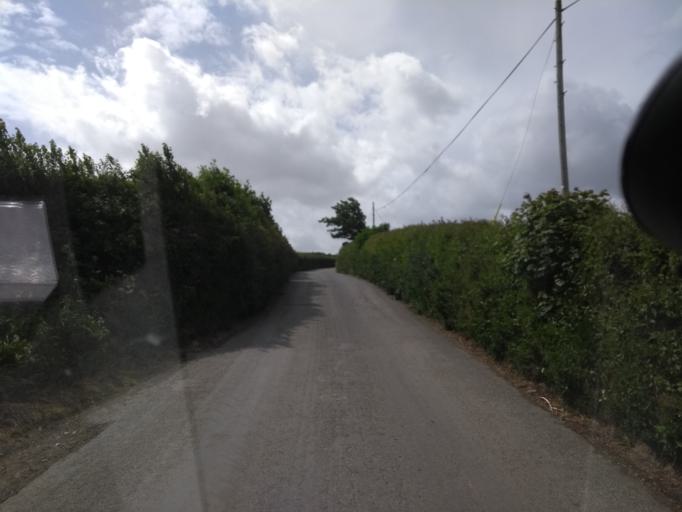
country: GB
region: England
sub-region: Somerset
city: Bridgwater
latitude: 51.1814
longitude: -3.0777
